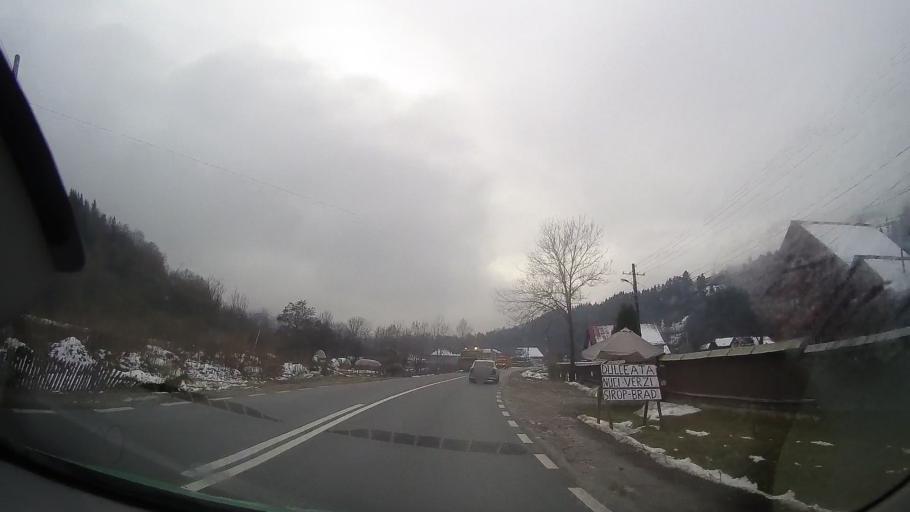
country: RO
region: Neamt
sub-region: Comuna Bicazu Ardelean
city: Bicazu Ardelean
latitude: 46.8646
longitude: 25.9405
